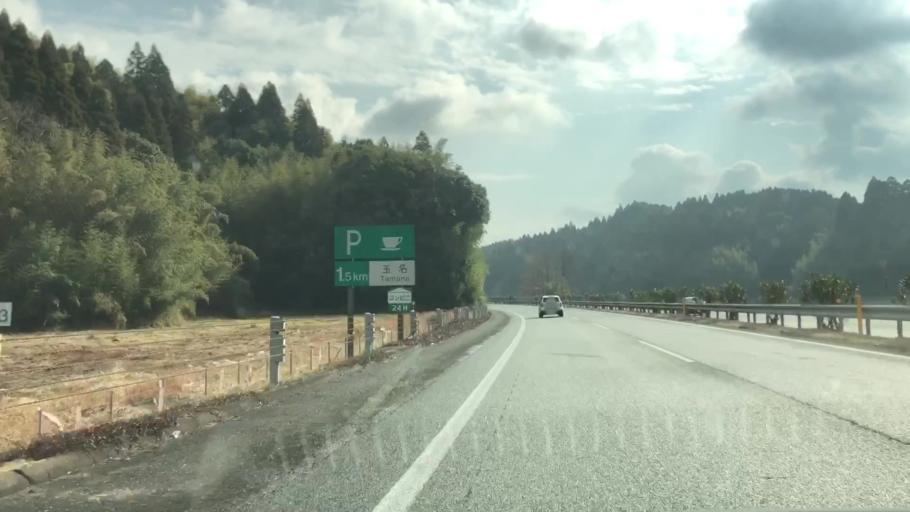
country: JP
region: Kumamoto
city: Yamaga
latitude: 33.0255
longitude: 130.5772
